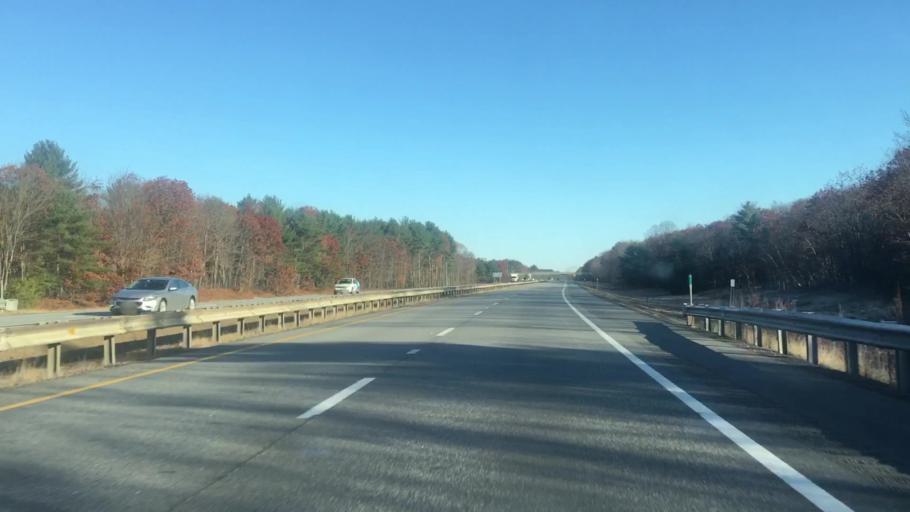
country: US
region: Maine
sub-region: Cumberland County
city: New Gloucester
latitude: 43.9522
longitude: -70.3316
